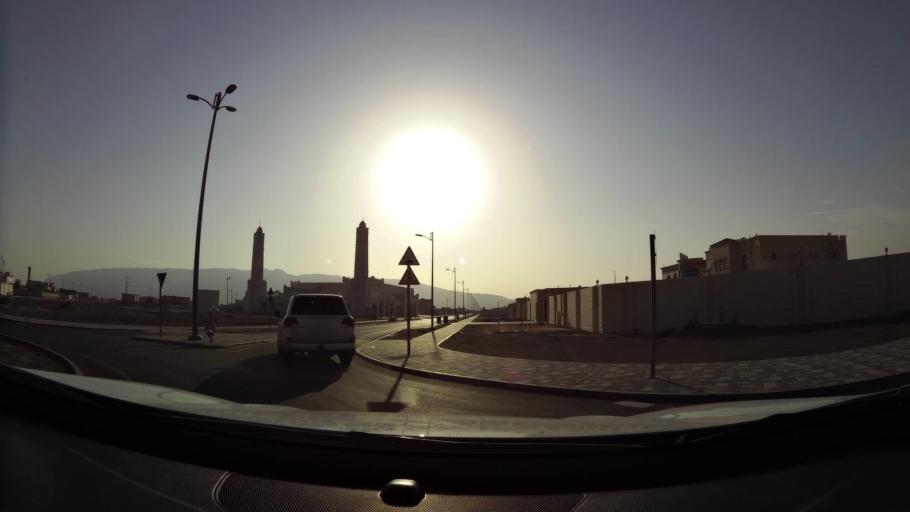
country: AE
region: Abu Dhabi
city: Al Ain
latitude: 24.1116
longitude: 55.8507
